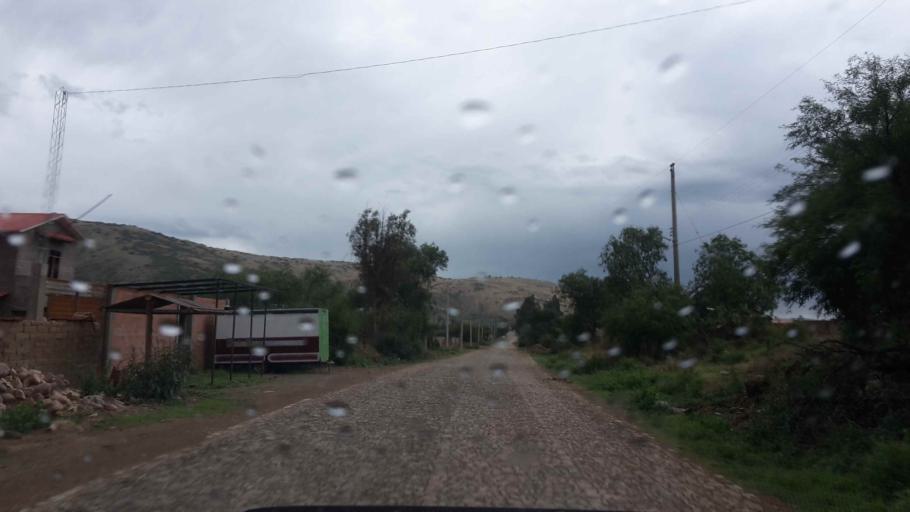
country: BO
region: Cochabamba
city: Tarata
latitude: -17.5495
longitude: -66.1673
